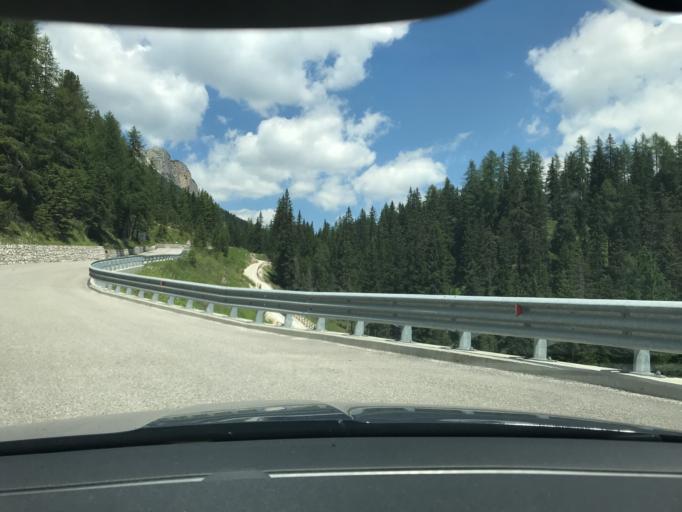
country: IT
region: Veneto
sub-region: Provincia di Belluno
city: Cortina d'Ampezzo
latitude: 46.5660
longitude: 12.2457
